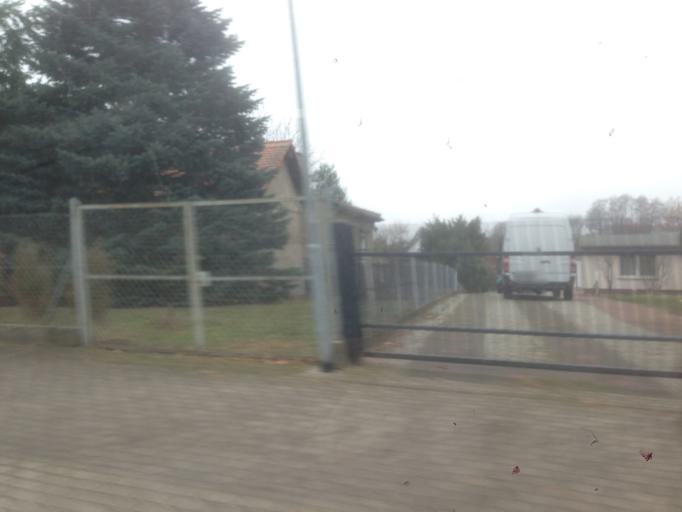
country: DE
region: Berlin
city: Blankenfelde
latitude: 52.6426
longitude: 13.3764
